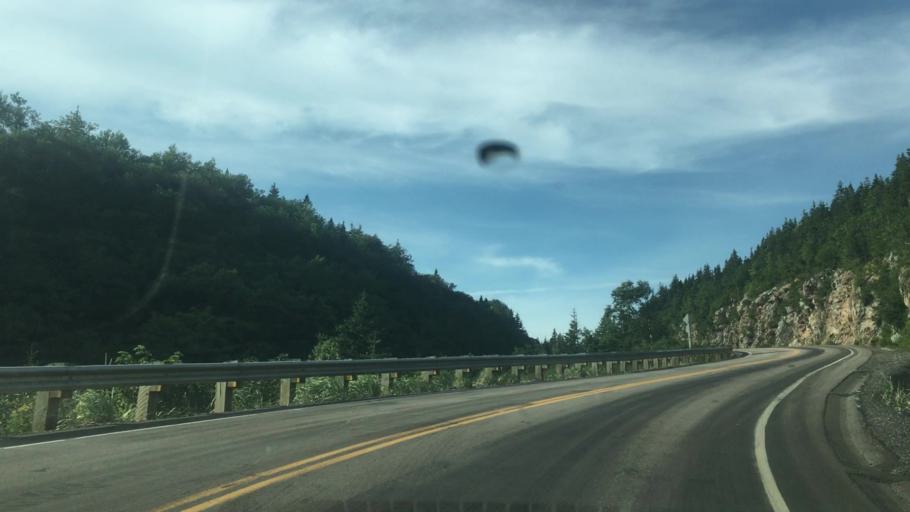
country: CA
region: Nova Scotia
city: Sydney Mines
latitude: 46.8211
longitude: -60.6543
